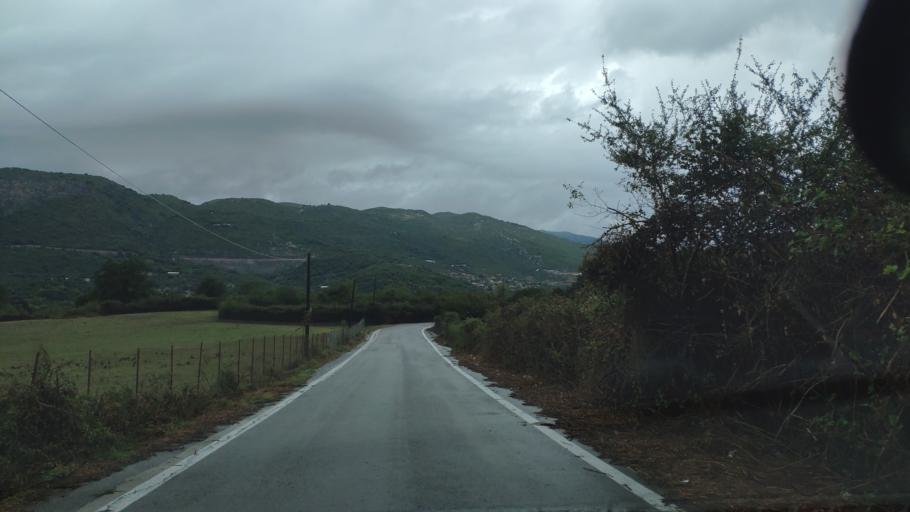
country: GR
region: Central Greece
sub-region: Nomos Evrytanias
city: Kerasochori
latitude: 39.1028
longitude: 21.4289
